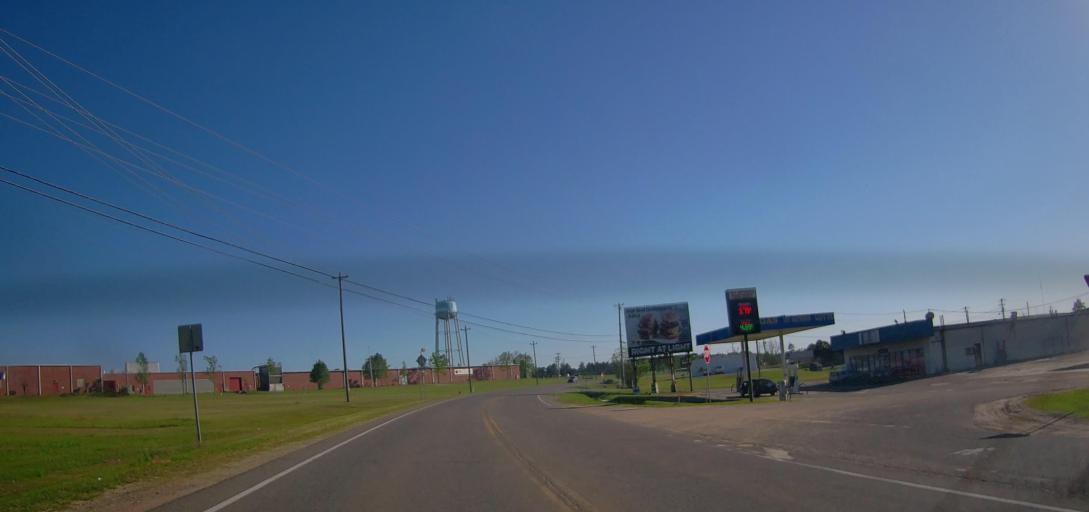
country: US
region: Georgia
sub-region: Ben Hill County
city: Fitzgerald
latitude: 31.6969
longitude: -83.2393
